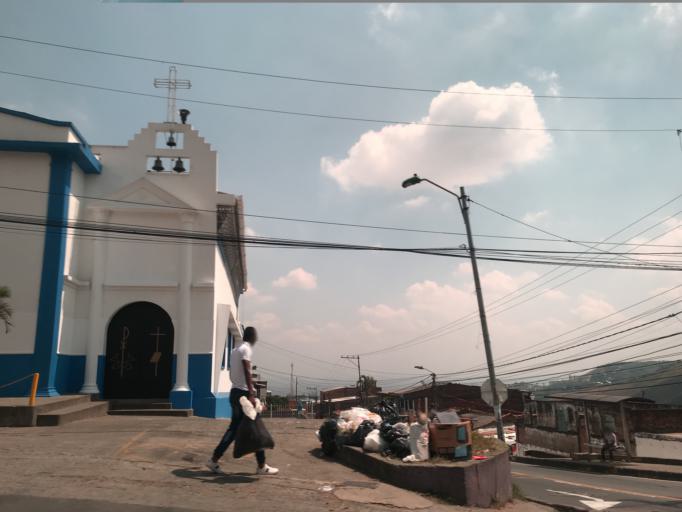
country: CO
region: Valle del Cauca
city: Cali
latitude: 3.4533
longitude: -76.5705
